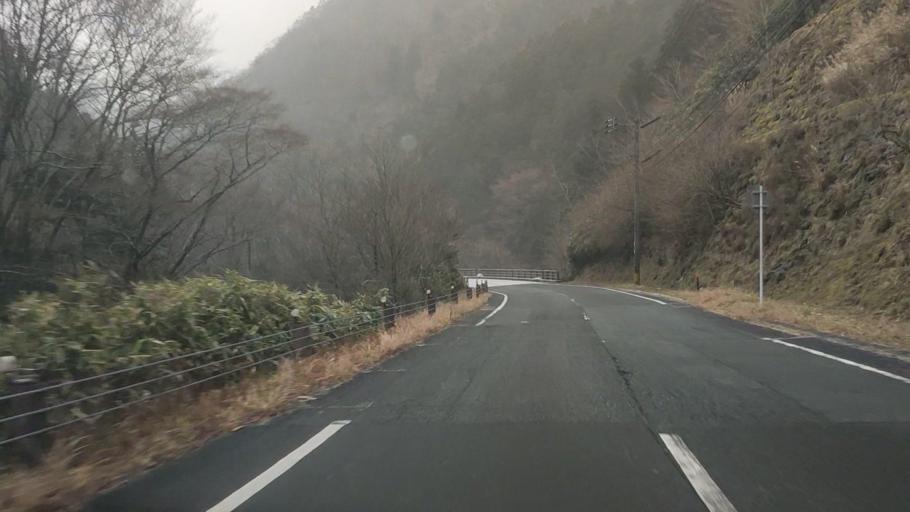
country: JP
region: Kumamoto
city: Matsubase
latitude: 32.5644
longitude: 130.9135
